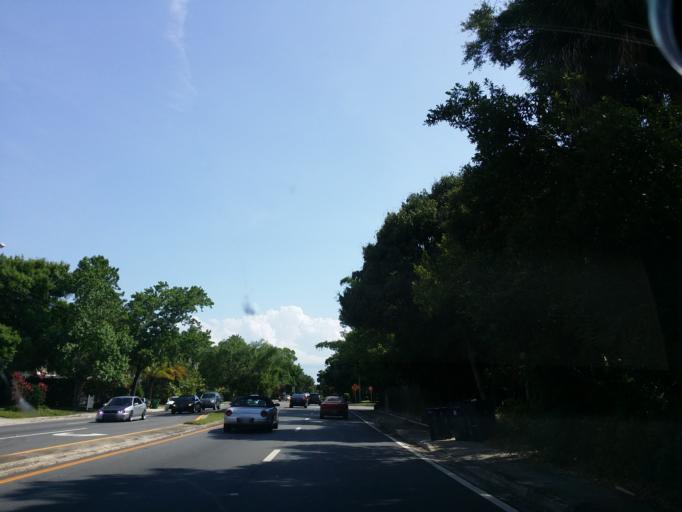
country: US
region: Florida
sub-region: Hillsborough County
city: Tampa
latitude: 27.9410
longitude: -82.5243
